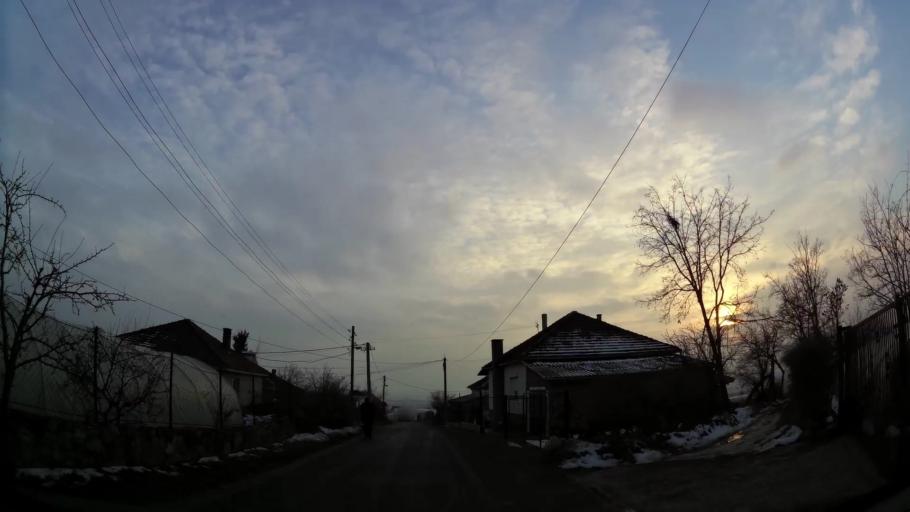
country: MK
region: Aracinovo
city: Arachinovo
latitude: 42.0327
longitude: 21.5464
